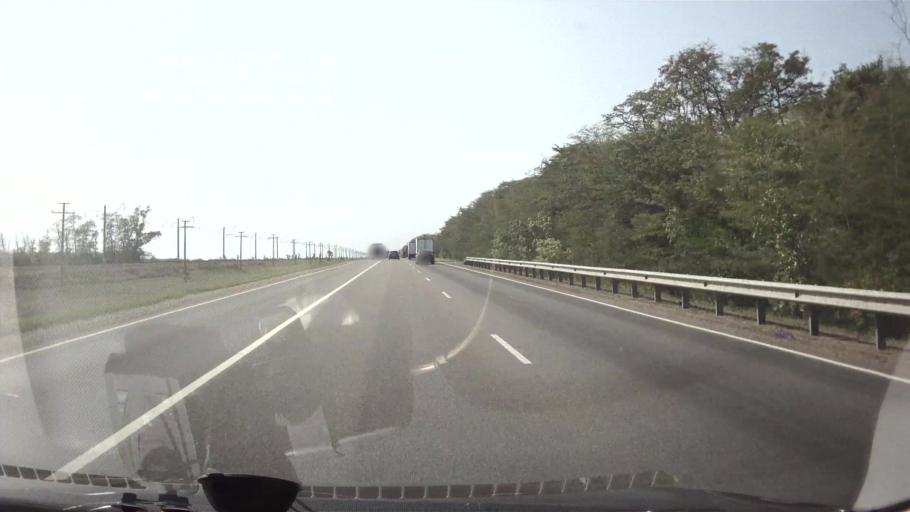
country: RU
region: Krasnodarskiy
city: Dvubratskiy
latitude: 45.2895
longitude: 39.8632
